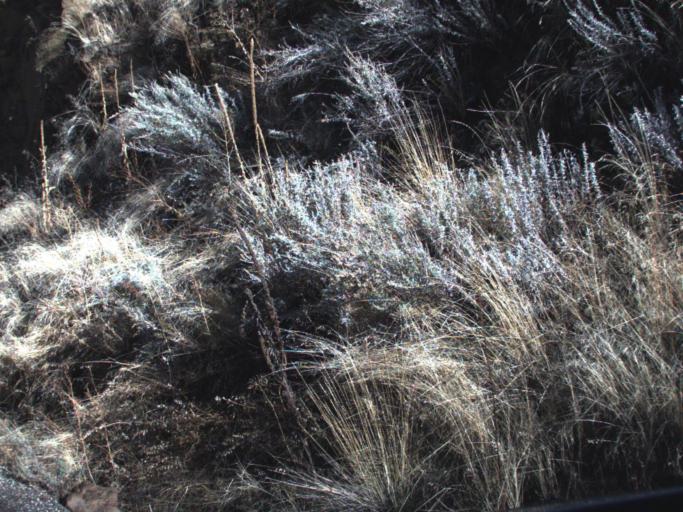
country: US
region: Washington
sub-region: Asotin County
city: Asotin
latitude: 46.0533
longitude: -117.2303
